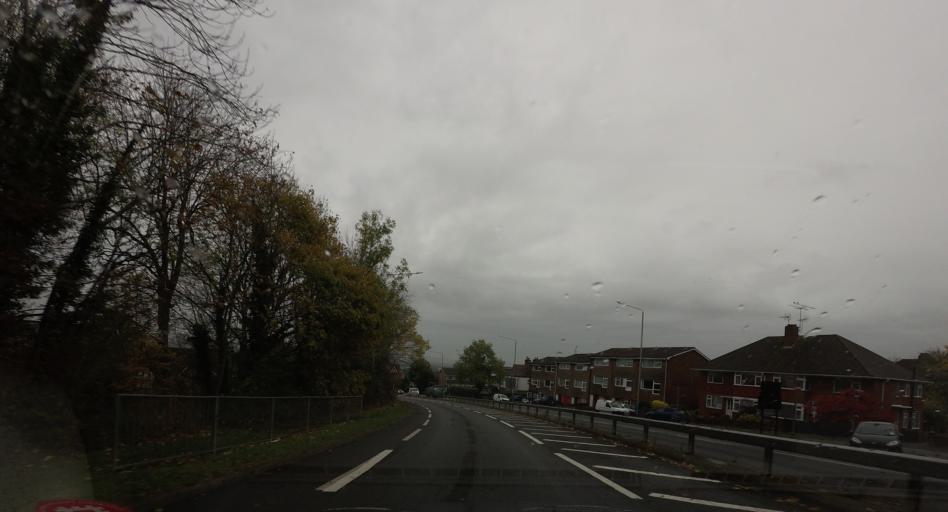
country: GB
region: England
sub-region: Kent
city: Tonbridge
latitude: 51.1834
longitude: 0.2647
